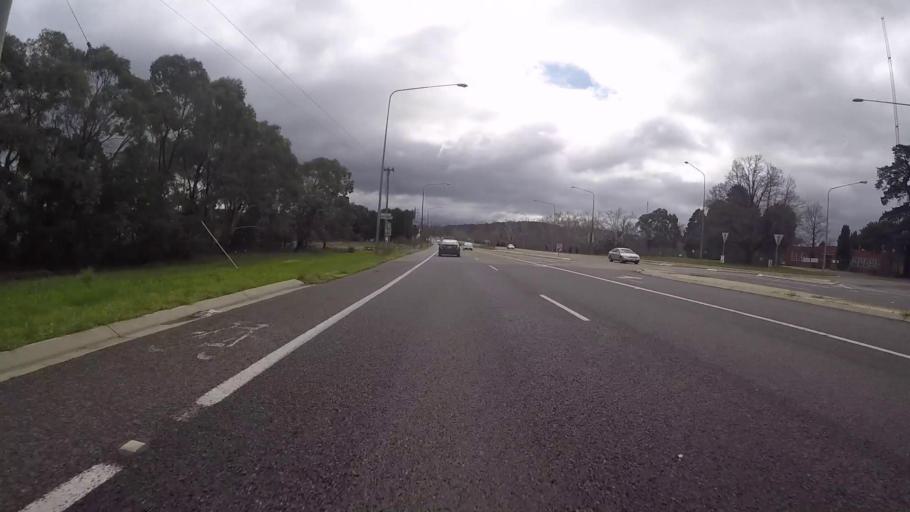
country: AU
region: Australian Capital Territory
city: Kaleen
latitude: -35.2199
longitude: 149.1191
